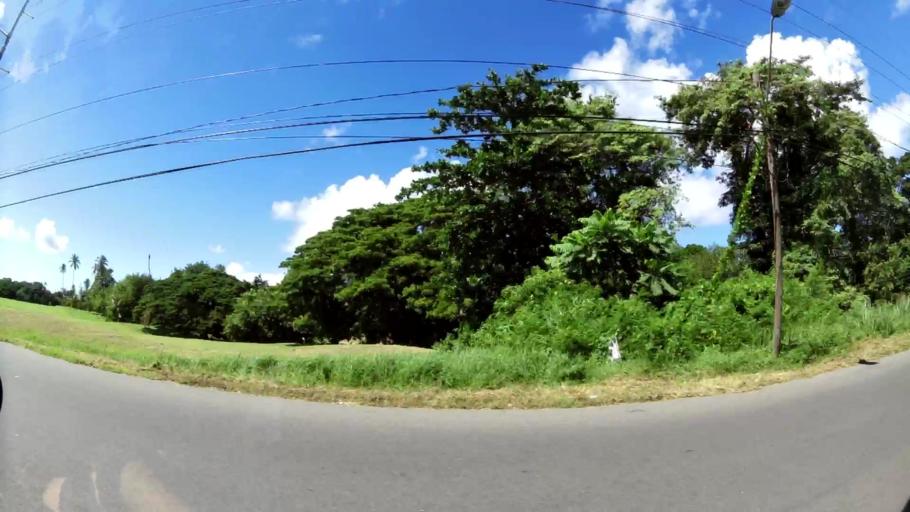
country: TT
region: Tobago
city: Scarborough
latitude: 11.1853
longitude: -60.7988
